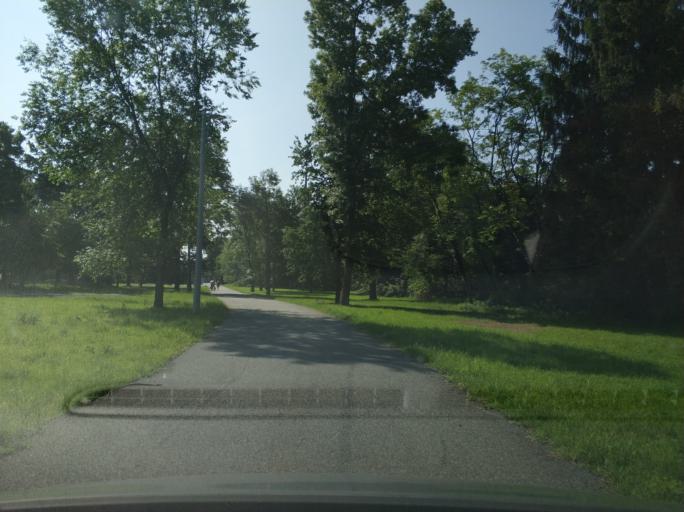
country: IT
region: Piedmont
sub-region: Provincia di Torino
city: Cafasse
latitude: 45.2484
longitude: 7.5260
